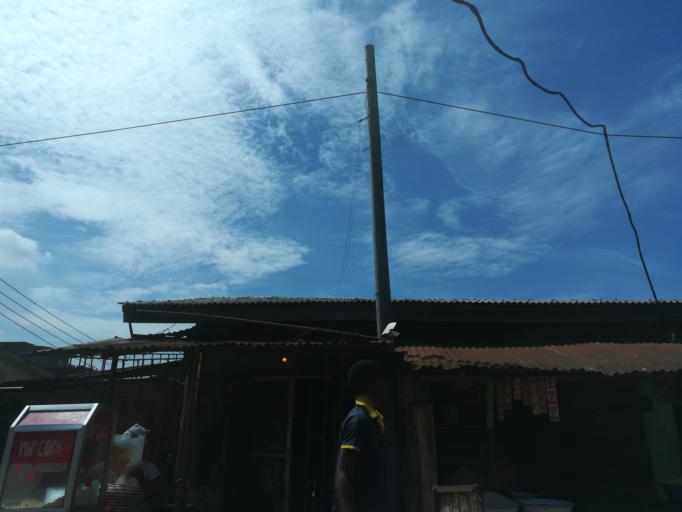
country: NG
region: Lagos
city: Oshodi
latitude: 6.5617
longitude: 3.3323
